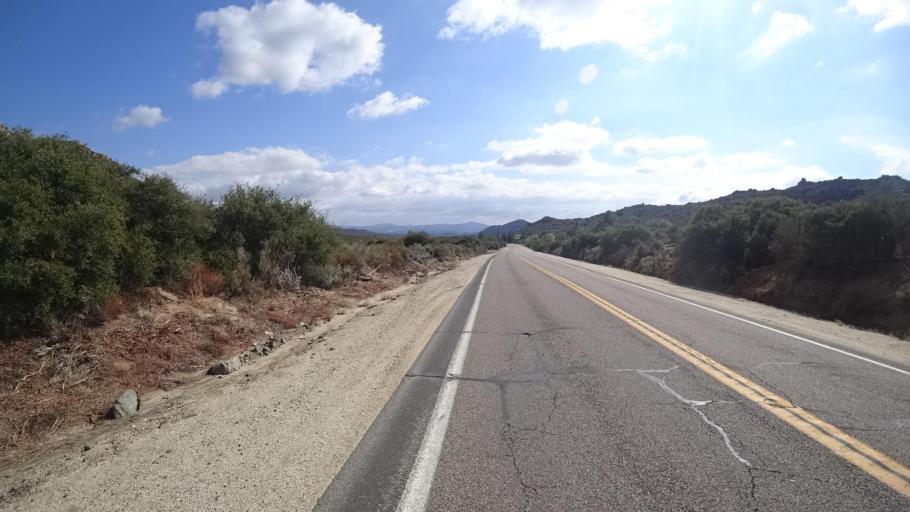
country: US
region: California
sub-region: San Diego County
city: Campo
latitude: 32.6860
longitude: -116.4883
